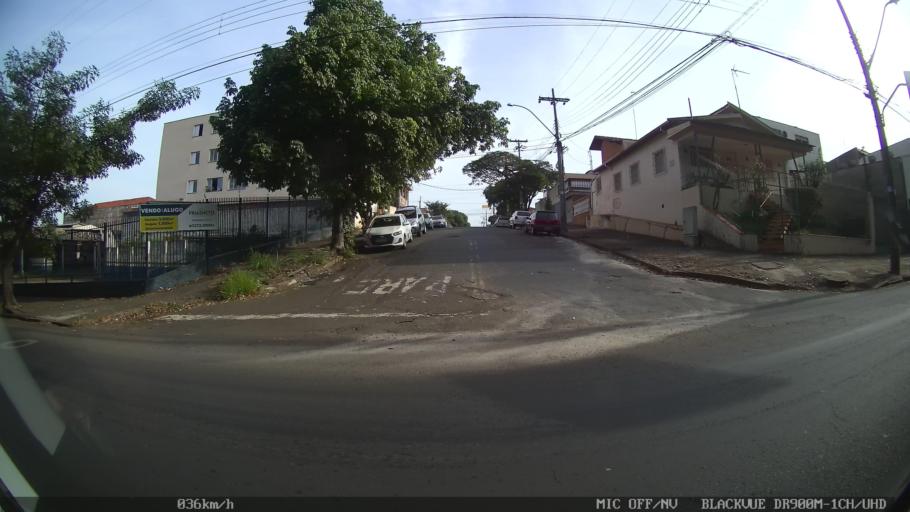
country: BR
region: Sao Paulo
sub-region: Piracicaba
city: Piracicaba
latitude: -22.7039
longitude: -47.6547
